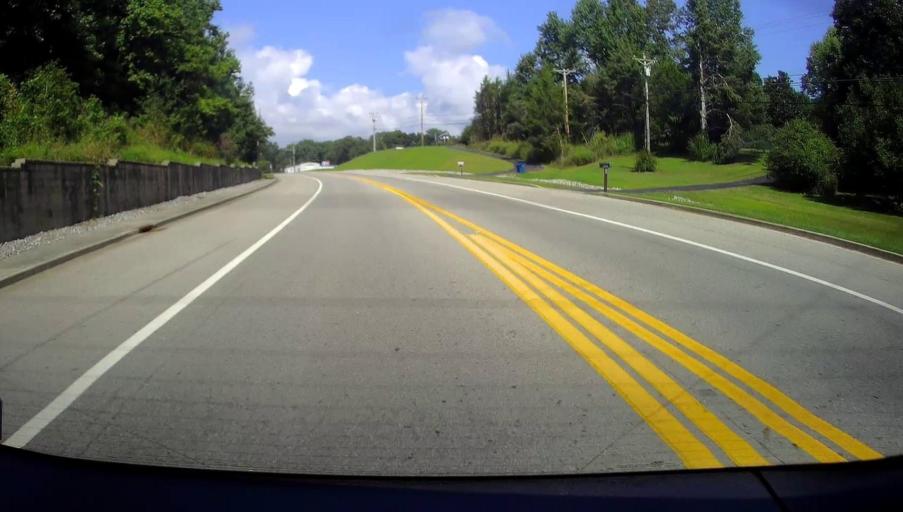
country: US
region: Tennessee
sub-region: Coffee County
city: Manchester
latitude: 35.4971
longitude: -86.1055
